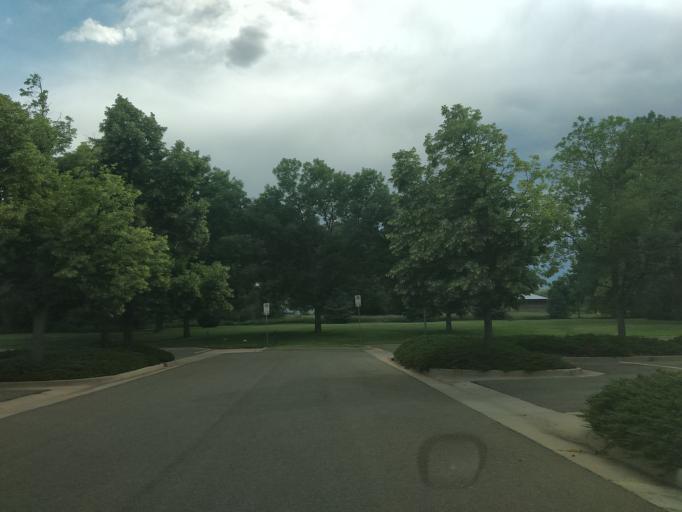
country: US
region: Colorado
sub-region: Jefferson County
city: Lakewood
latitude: 39.7045
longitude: -105.1026
